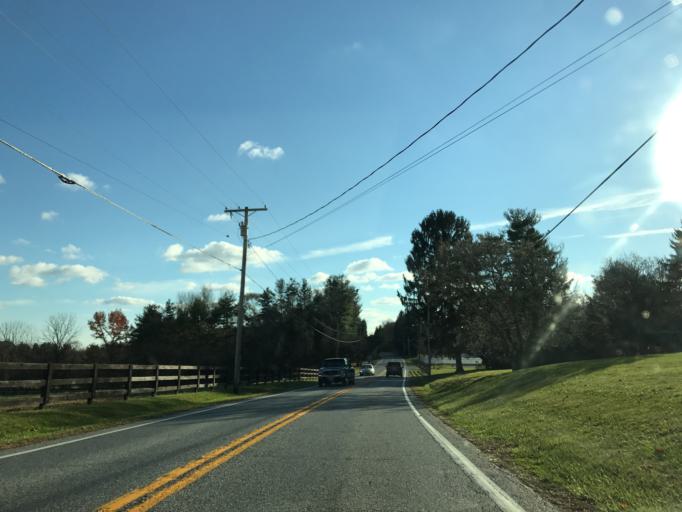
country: US
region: Maryland
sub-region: Harford County
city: Jarrettsville
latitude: 39.6035
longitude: -76.5124
